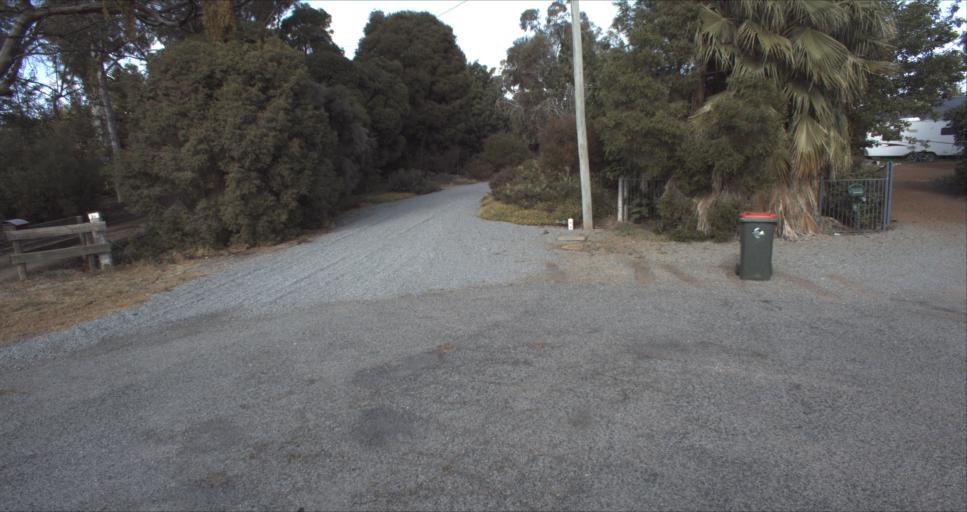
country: AU
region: New South Wales
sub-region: Leeton
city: Leeton
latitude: -34.5682
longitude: 146.3916
